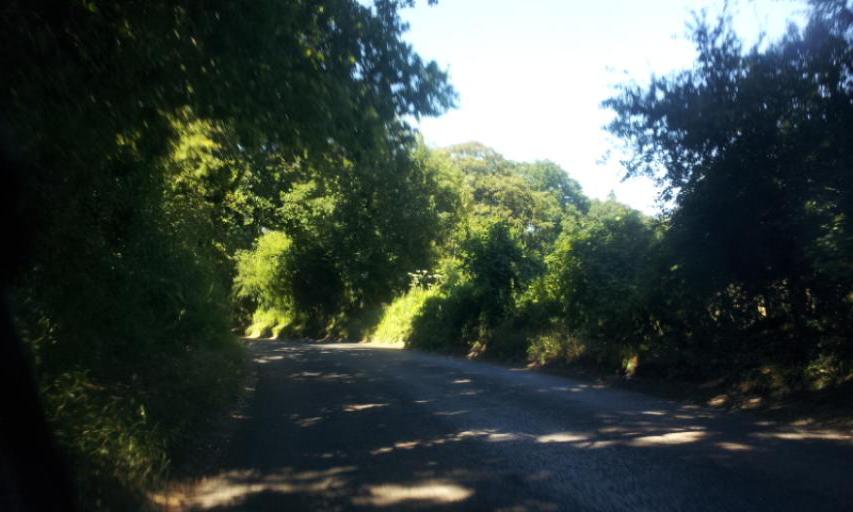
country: GB
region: England
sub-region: Kent
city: Sittingbourne
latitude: 51.3084
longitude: 0.7403
